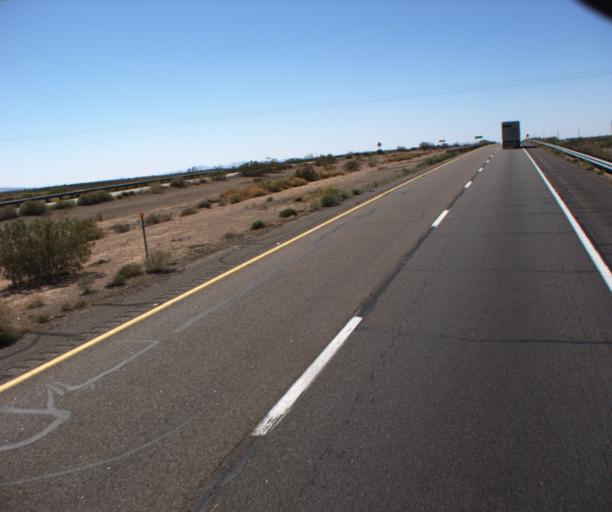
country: US
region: Arizona
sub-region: Maricopa County
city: Gila Bend
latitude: 32.8589
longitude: -113.2107
